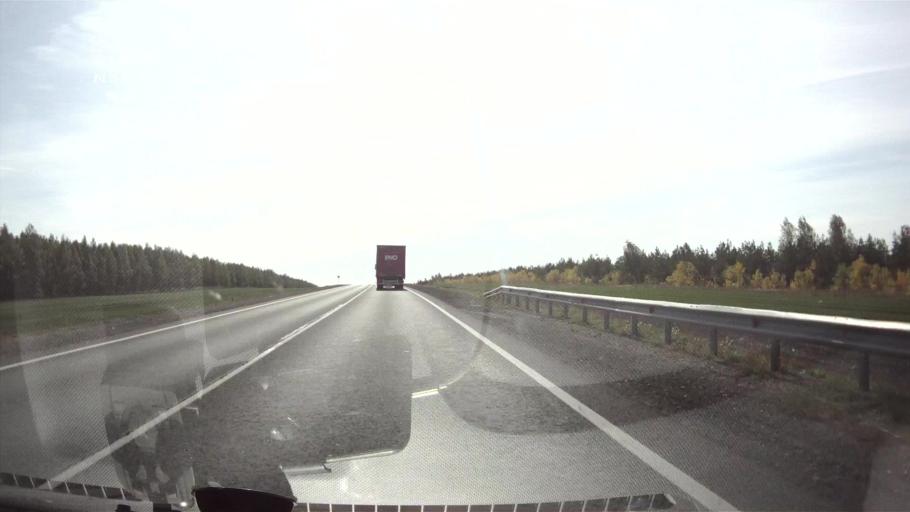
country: RU
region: Samara
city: Syzran'
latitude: 52.8964
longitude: 48.2955
